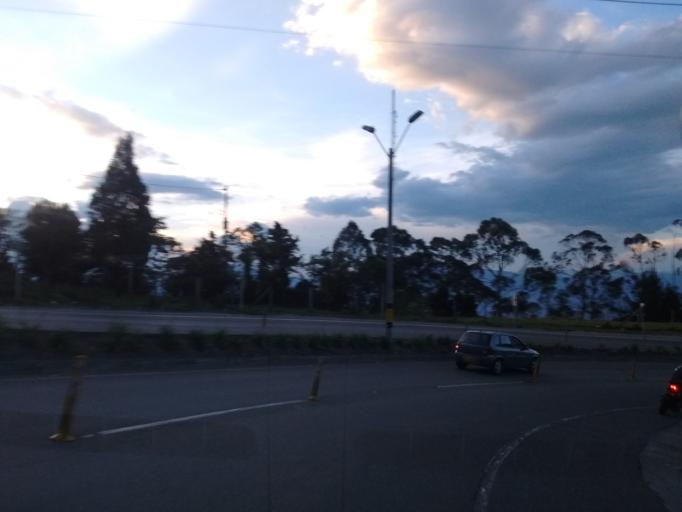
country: CO
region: Antioquia
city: Envigado
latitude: 6.1523
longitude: -75.5466
